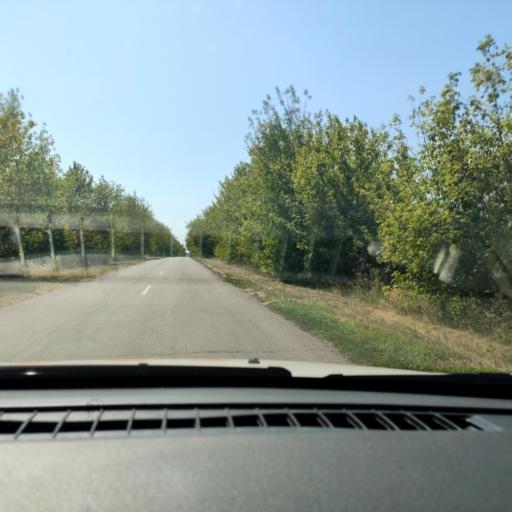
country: RU
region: Voronezj
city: Imeni Pervogo Maya
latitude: 50.7156
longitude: 39.3458
